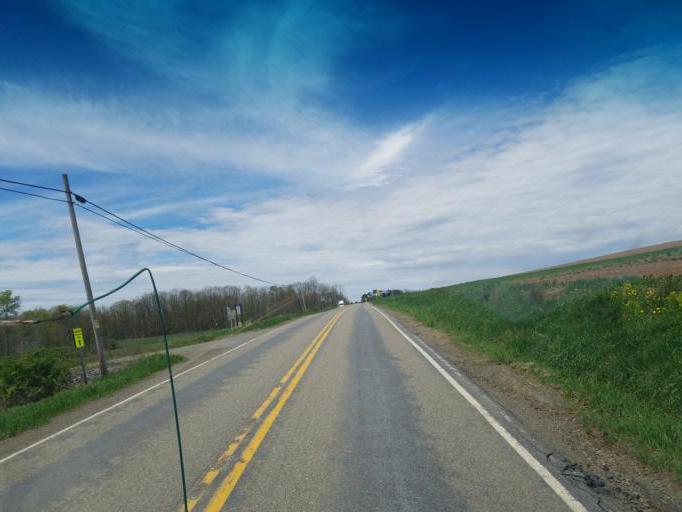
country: US
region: Pennsylvania
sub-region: Tioga County
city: Wellsboro
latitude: 41.7050
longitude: -77.4082
